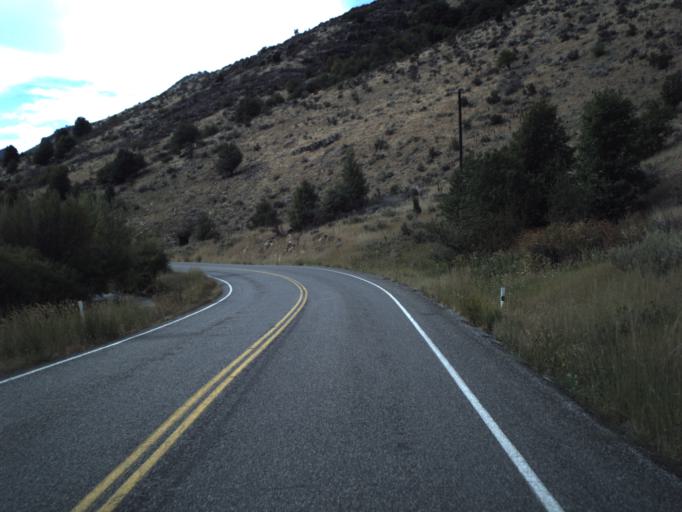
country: US
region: Utah
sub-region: Cache County
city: Millville
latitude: 41.6083
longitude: -111.6207
